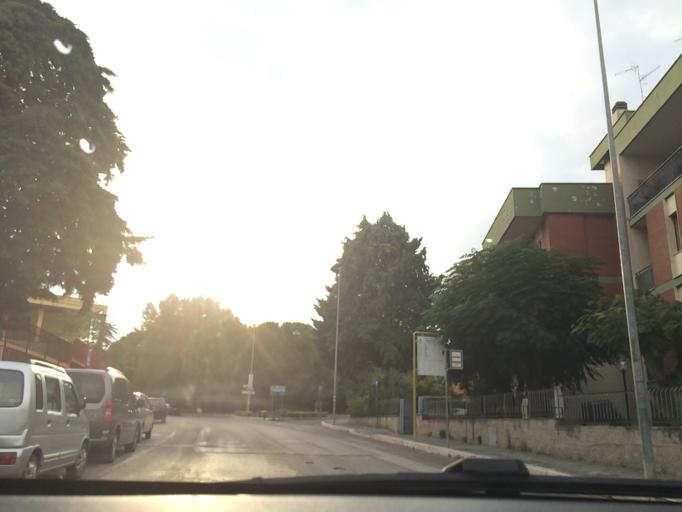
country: IT
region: Basilicate
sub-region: Provincia di Matera
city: Matera
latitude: 40.6636
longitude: 16.5964
